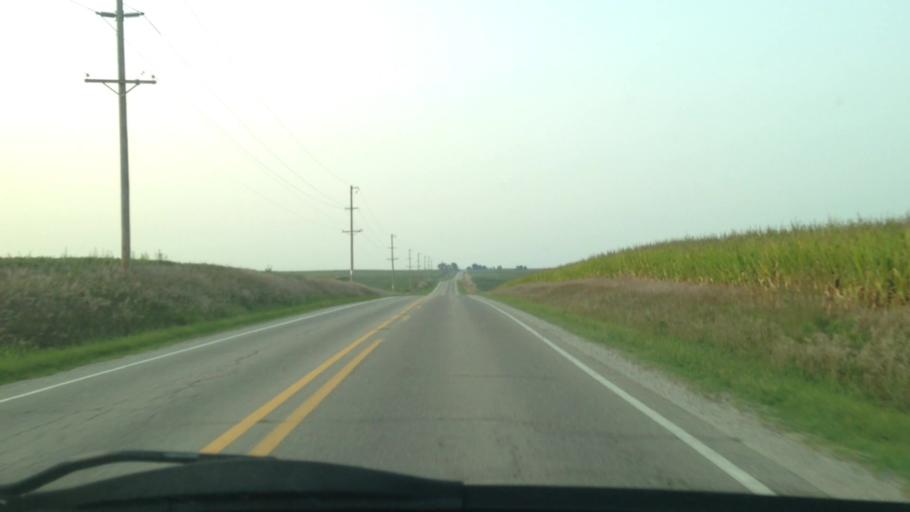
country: US
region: Iowa
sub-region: Iowa County
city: Marengo
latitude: 41.9436
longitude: -92.0850
